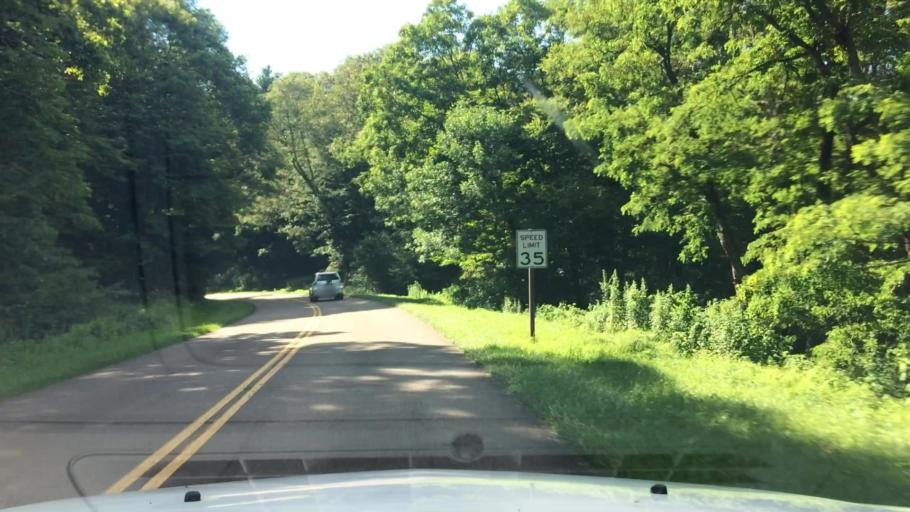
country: US
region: North Carolina
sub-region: Watauga County
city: Blowing Rock
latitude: 36.1481
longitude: -81.7014
